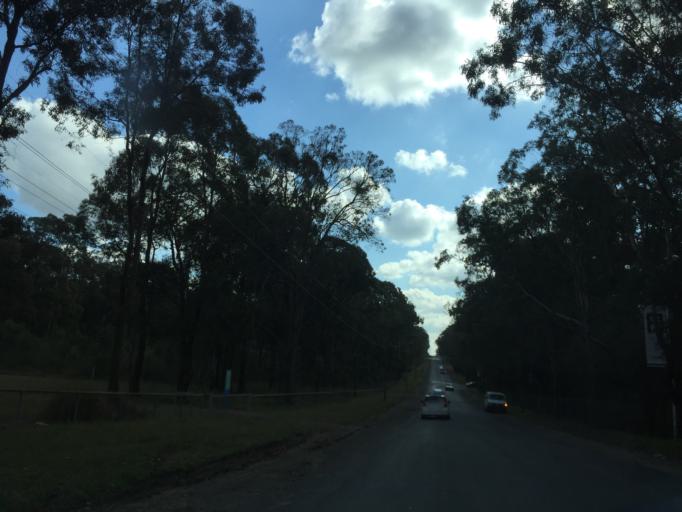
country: AU
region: New South Wales
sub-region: Blacktown
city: Rouse Hill
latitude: -33.6882
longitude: 150.9050
